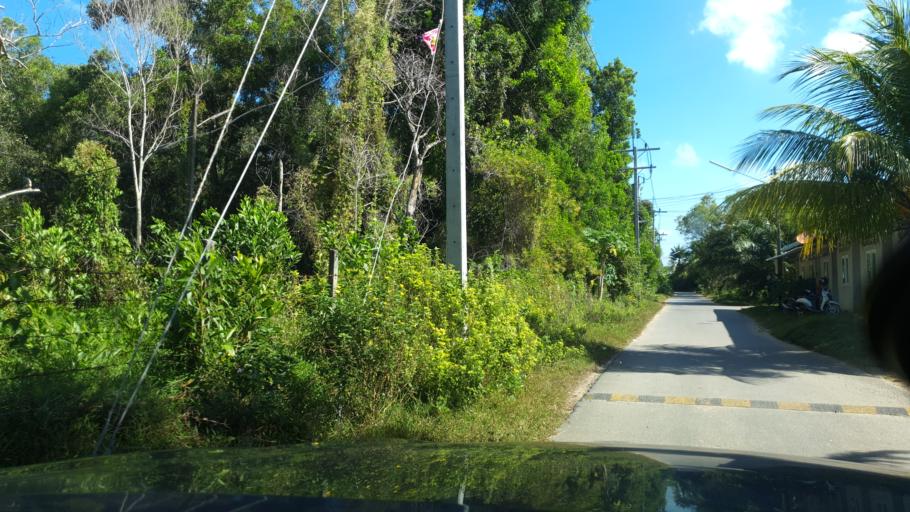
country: TH
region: Krabi
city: Krabi
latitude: 8.0250
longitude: 98.8793
